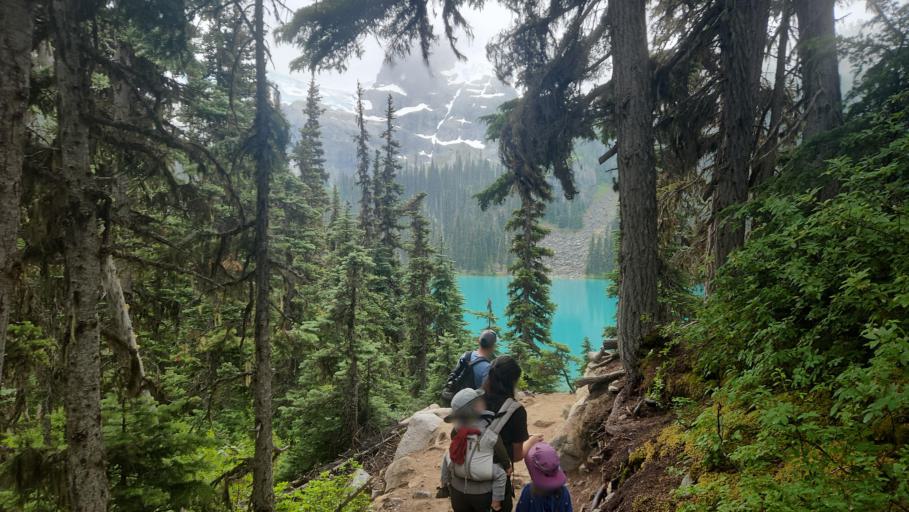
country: CA
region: British Columbia
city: Pemberton
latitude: 50.3530
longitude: -122.4837
